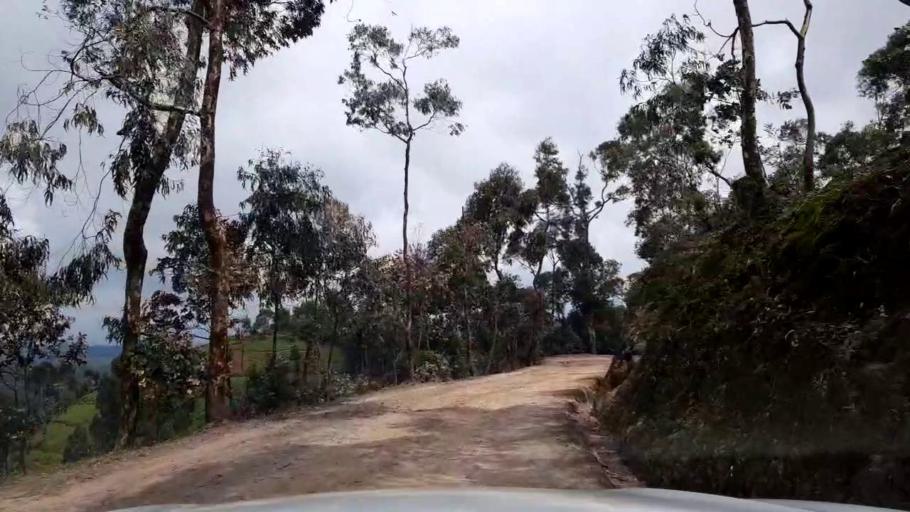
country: RW
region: Western Province
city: Kibuye
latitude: -1.9388
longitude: 29.4656
